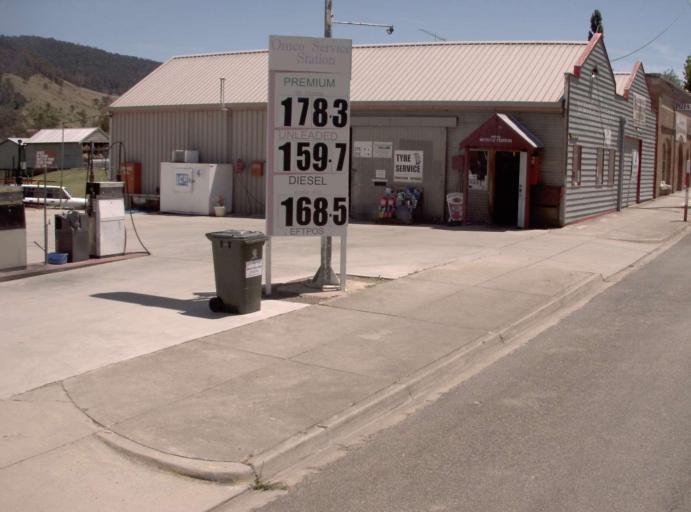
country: AU
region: Victoria
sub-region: Alpine
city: Mount Beauty
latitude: -37.1003
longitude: 147.5928
